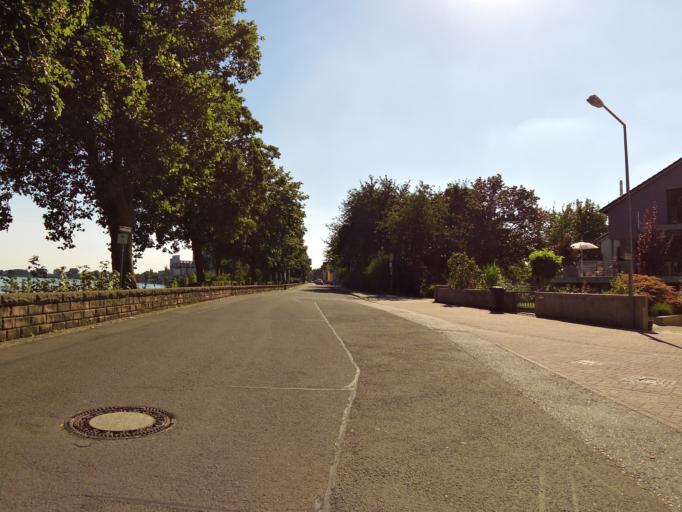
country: DE
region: Rheinland-Pfalz
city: Osthofen
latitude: 49.6960
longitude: 8.3571
